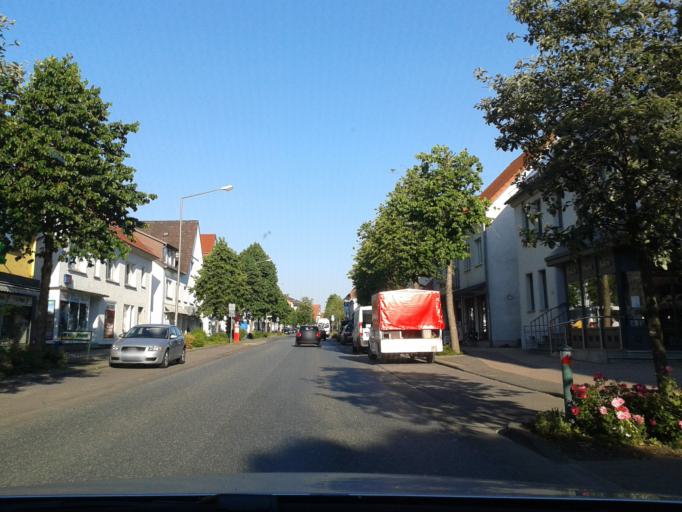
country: DE
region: North Rhine-Westphalia
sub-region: Regierungsbezirk Detmold
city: Barntrup
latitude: 51.9906
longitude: 9.1141
